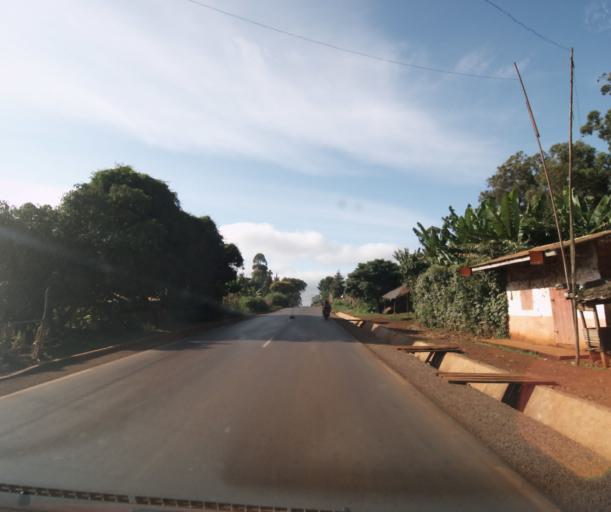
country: CM
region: West
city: Mbouda
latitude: 5.6123
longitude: 10.2873
